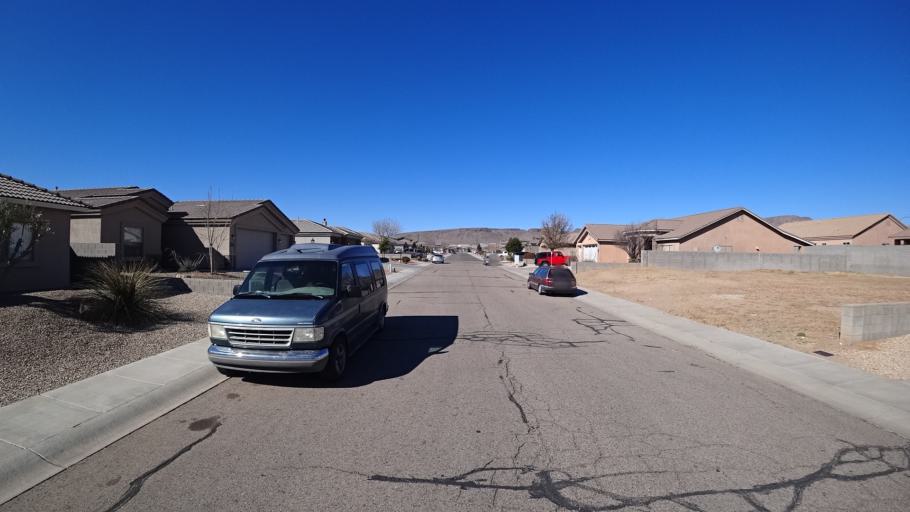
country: US
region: Arizona
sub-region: Mohave County
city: New Kingman-Butler
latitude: 35.2383
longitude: -114.0295
